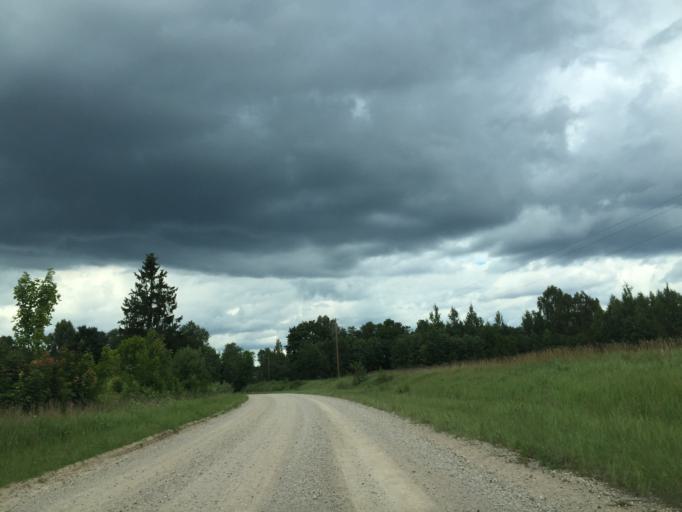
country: LV
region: Malpils
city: Malpils
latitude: 56.9326
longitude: 25.0143
